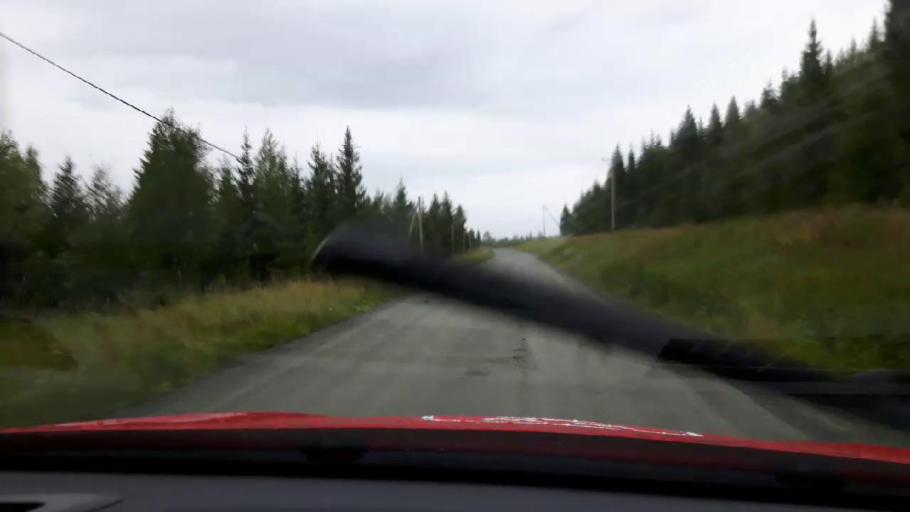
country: SE
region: Jaemtland
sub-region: Are Kommun
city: Are
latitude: 63.4103
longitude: 12.8310
